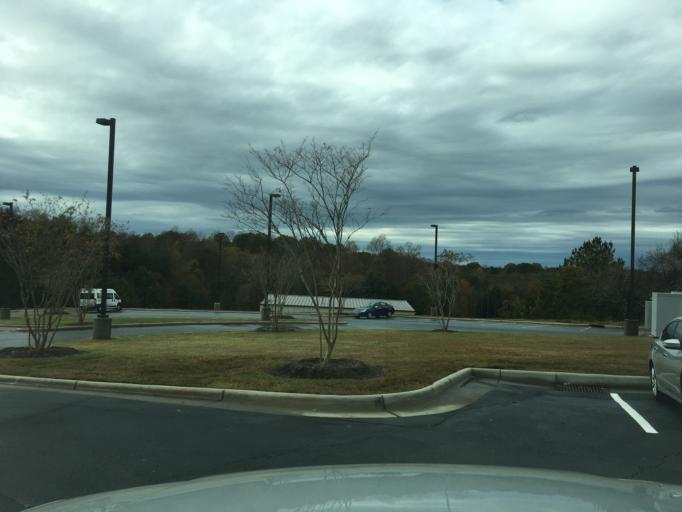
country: US
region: North Carolina
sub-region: Catawba County
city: Newton
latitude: 35.6613
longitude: -81.2324
